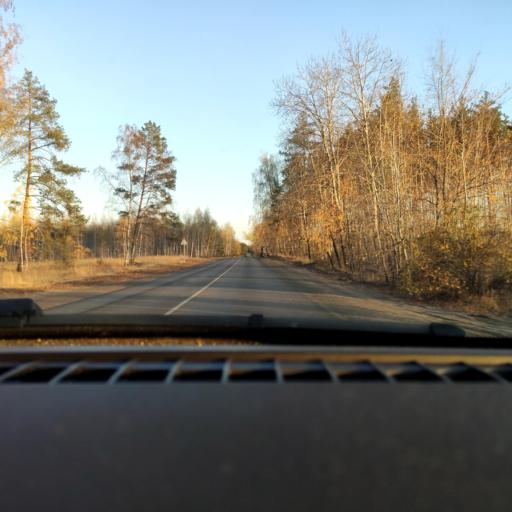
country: RU
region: Voronezj
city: Maslovka
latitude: 51.5811
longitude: 39.2807
